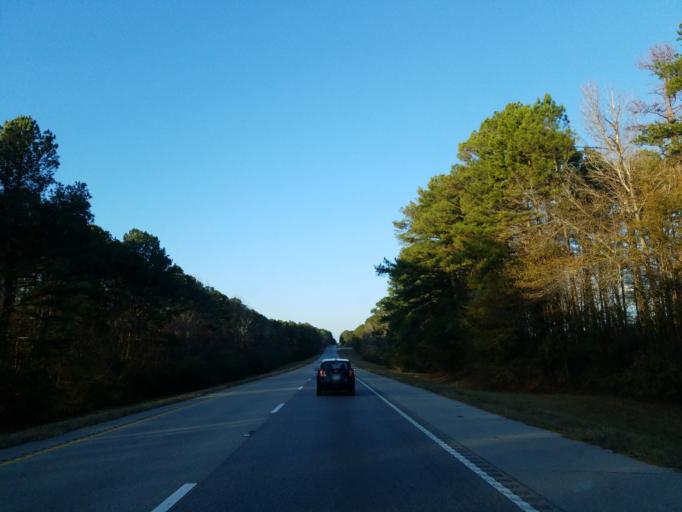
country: US
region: Mississippi
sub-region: Clarke County
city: Stonewall
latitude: 32.1553
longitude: -88.8676
